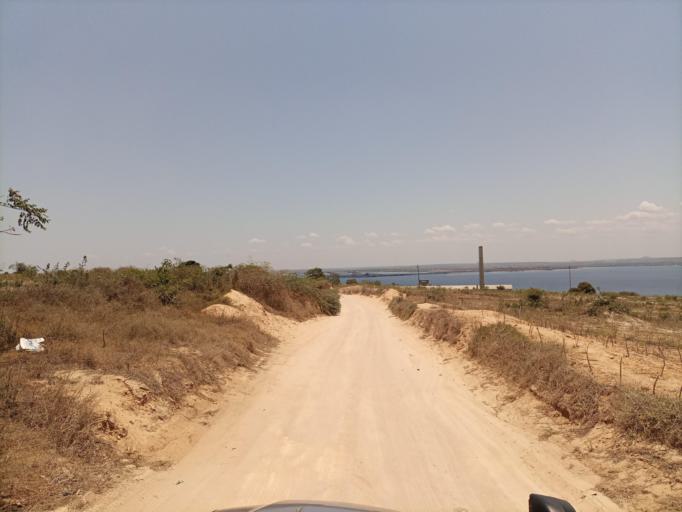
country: MZ
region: Nampula
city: Nacala
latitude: -14.5181
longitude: 40.6815
